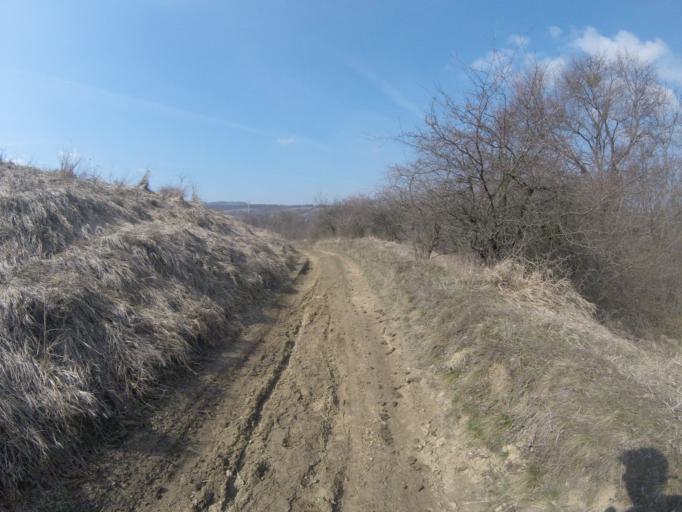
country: HU
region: Komarom-Esztergom
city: Nyergesujfalu
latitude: 47.7469
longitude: 18.5530
